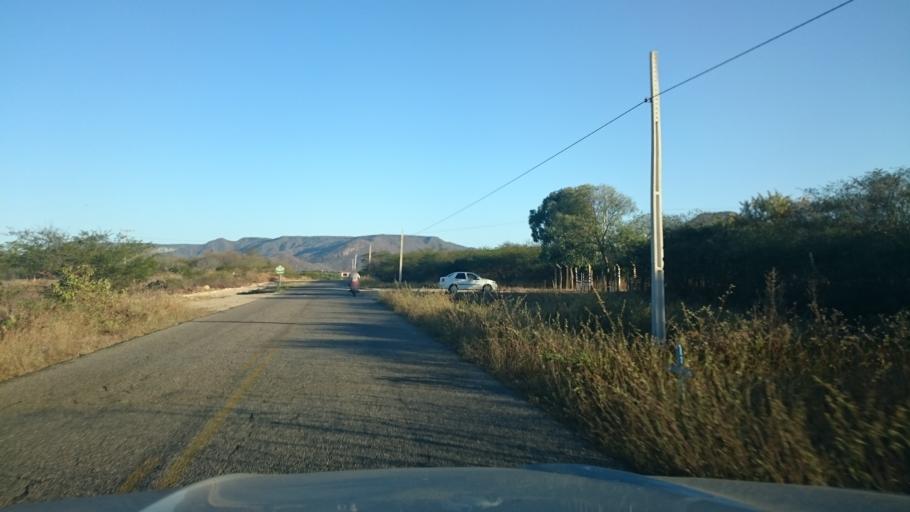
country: BR
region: Rio Grande do Norte
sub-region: Umarizal
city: Umarizal
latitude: -5.9730
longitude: -37.9512
